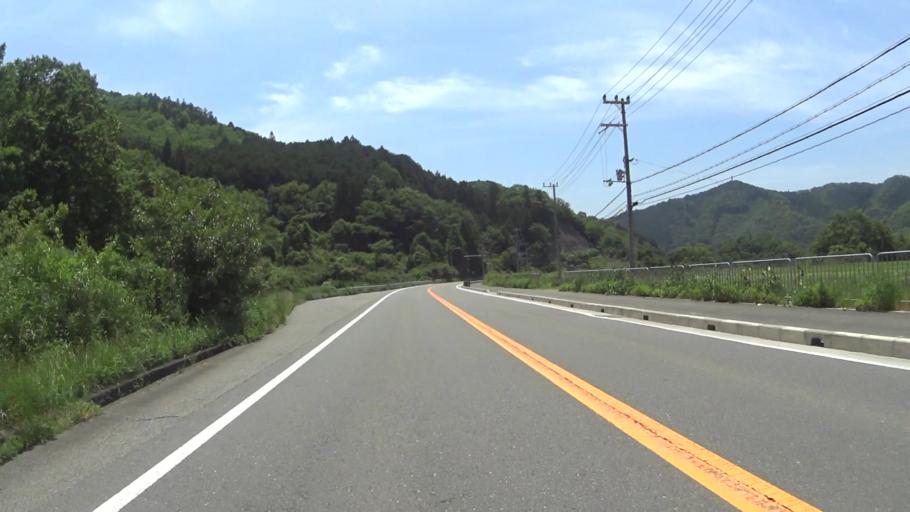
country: JP
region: Kyoto
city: Ayabe
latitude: 35.2062
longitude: 135.2666
